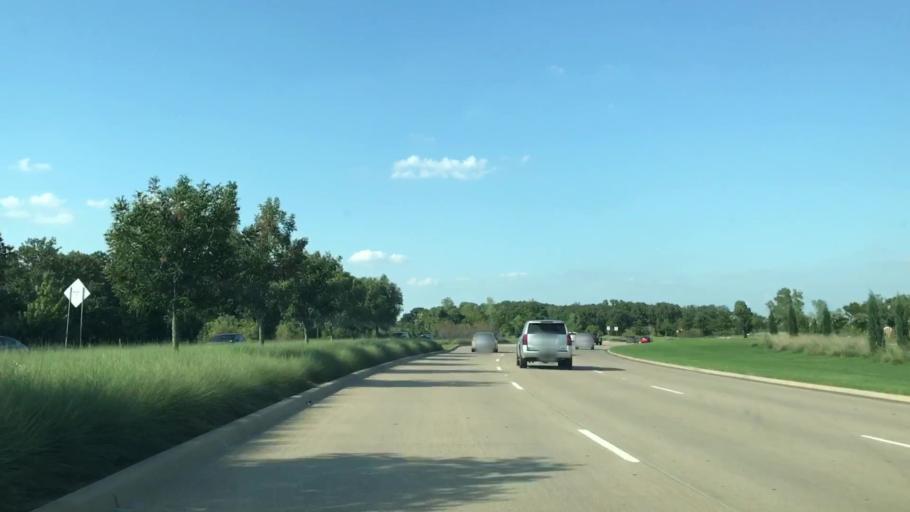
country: US
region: Texas
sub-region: Denton County
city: Trophy Club
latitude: 32.9826
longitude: -97.1853
